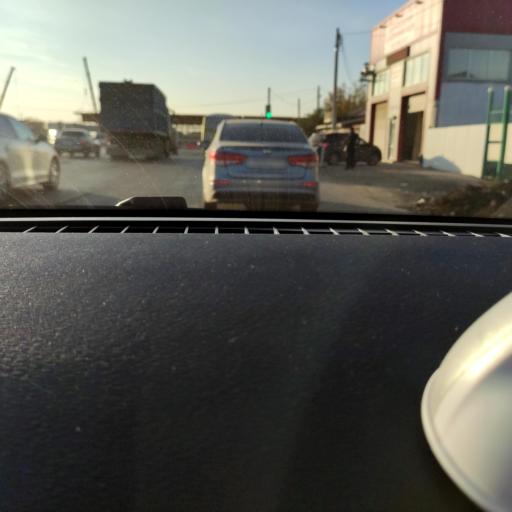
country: RU
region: Samara
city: Samara
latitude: 53.1360
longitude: 50.1051
